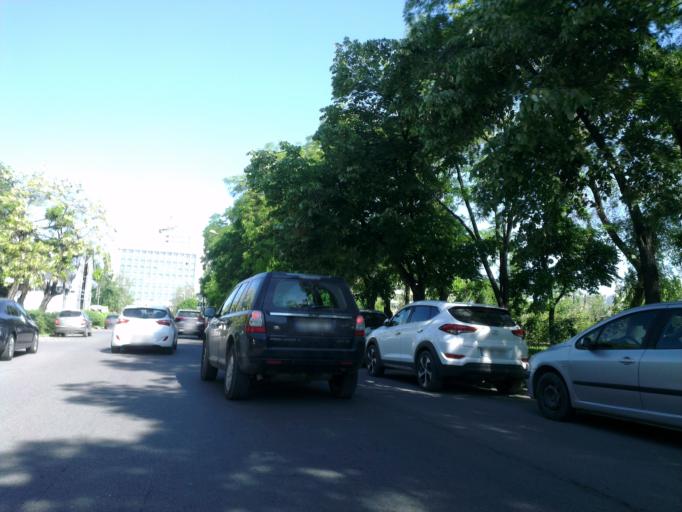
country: MD
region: Chisinau
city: Chisinau
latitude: 47.0291
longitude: 28.8413
